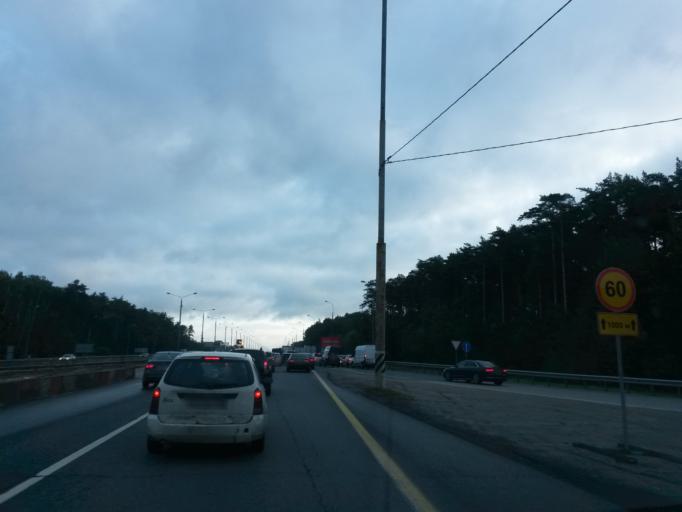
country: RU
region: Moskovskaya
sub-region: Podol'skiy Rayon
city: Podol'sk
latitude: 55.4083
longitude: 37.6067
